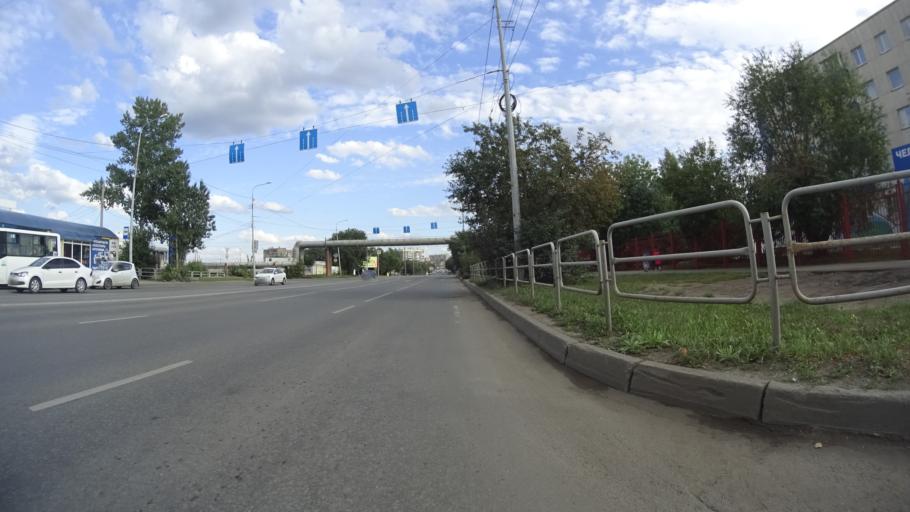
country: RU
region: Chelyabinsk
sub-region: Gorod Chelyabinsk
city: Chelyabinsk
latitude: 55.2028
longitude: 61.3256
